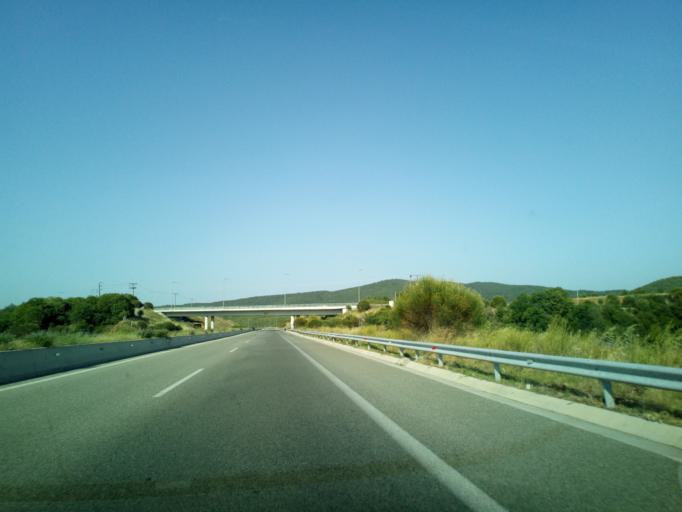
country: GR
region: Central Macedonia
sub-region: Nomos Thessalonikis
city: Stavros
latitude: 40.6779
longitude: 23.6089
